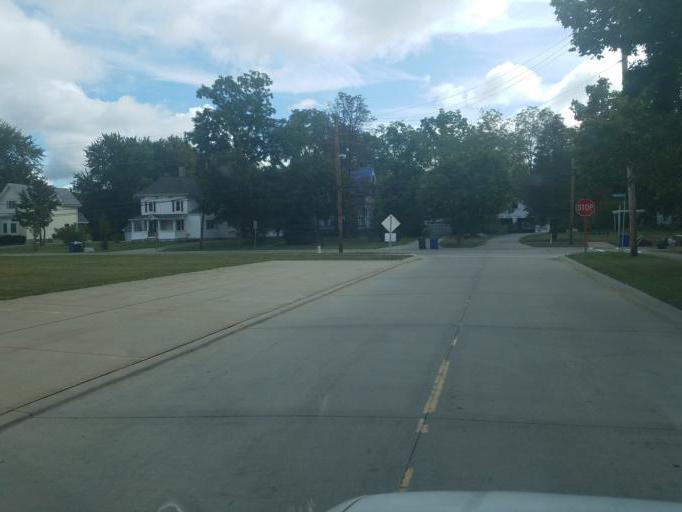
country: US
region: Ohio
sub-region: Lorain County
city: Wellington
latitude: 41.1646
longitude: -82.2156
